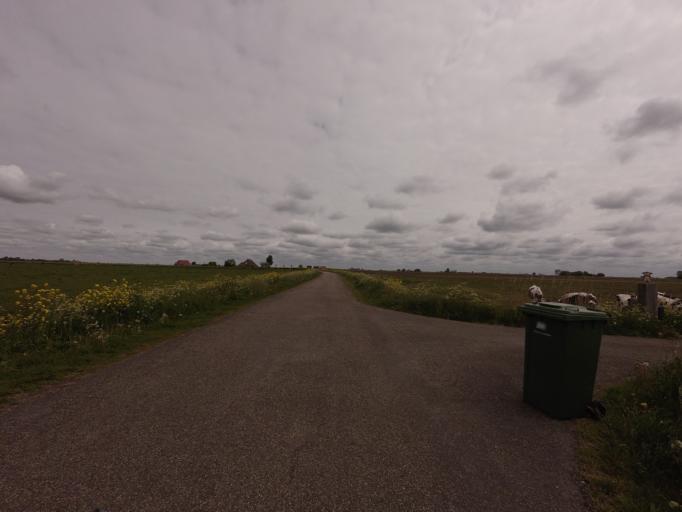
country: NL
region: Friesland
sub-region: Sudwest Fryslan
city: Workum
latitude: 52.9612
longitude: 5.4841
